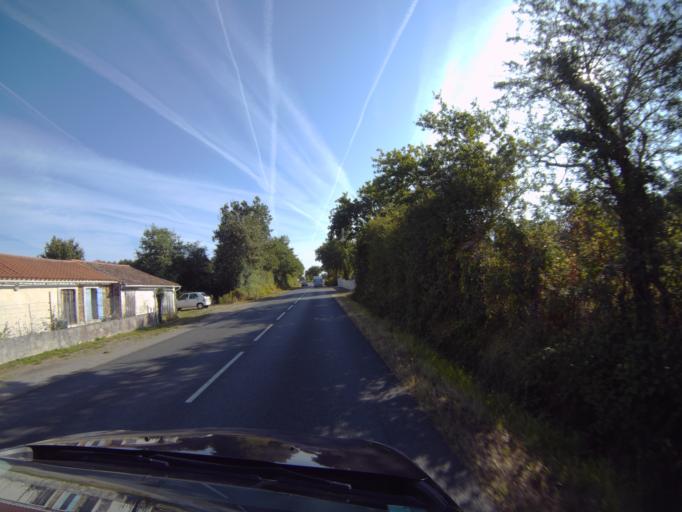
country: FR
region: Pays de la Loire
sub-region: Departement de la Vendee
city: Grosbreuil
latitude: 46.5146
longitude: -1.5619
